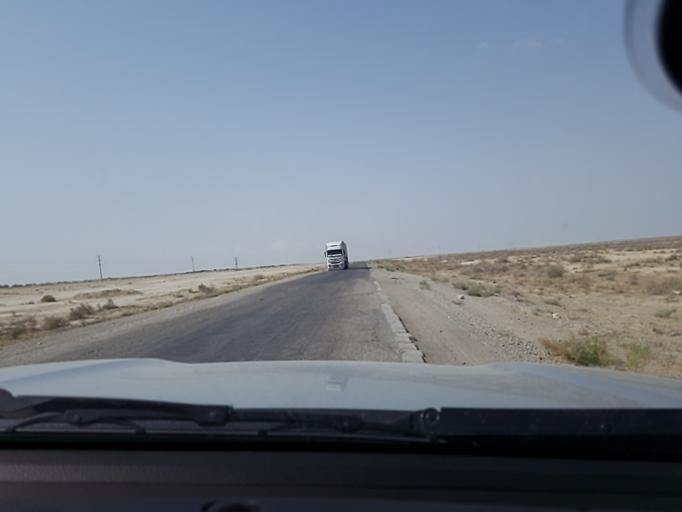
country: TM
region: Balkan
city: Gumdag
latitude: 38.7708
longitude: 54.5873
